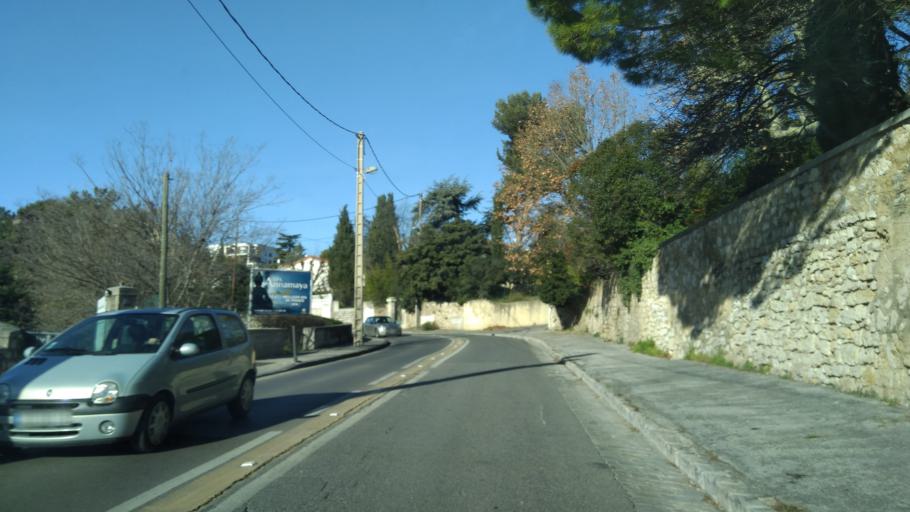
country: FR
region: Provence-Alpes-Cote d'Azur
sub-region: Departement des Bouches-du-Rhone
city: Marseille 12
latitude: 43.3036
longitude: 5.4417
